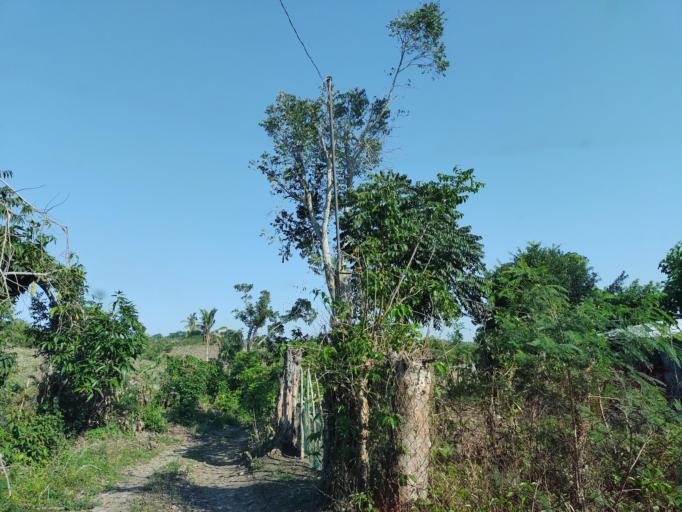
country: MX
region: Veracruz
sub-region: Papantla
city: Polutla
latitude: 20.4549
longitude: -97.2258
